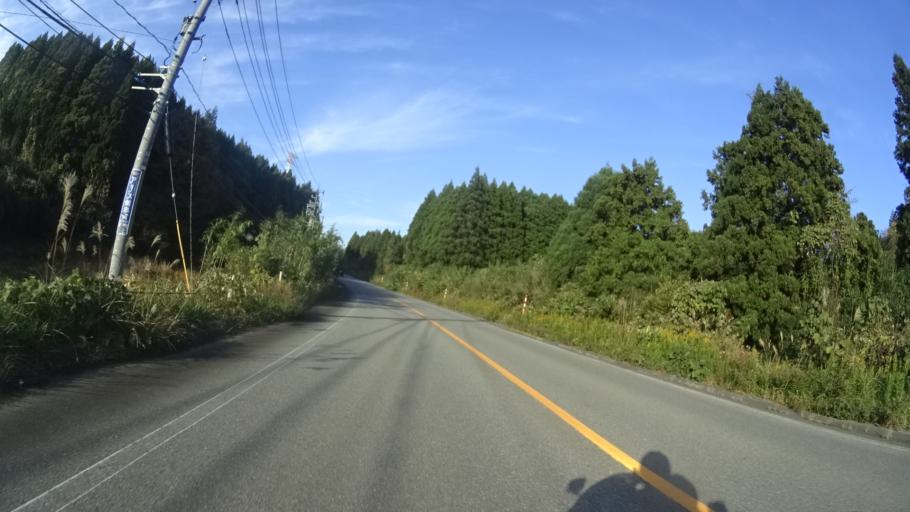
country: JP
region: Ishikawa
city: Hakui
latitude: 37.0597
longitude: 136.7794
